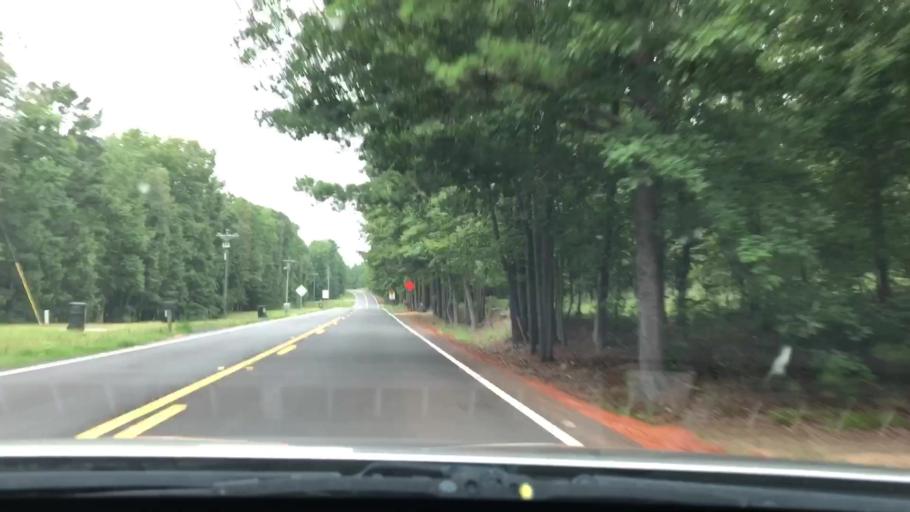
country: US
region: Georgia
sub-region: Upson County
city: Hannahs Mill
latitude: 33.0150
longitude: -84.4166
